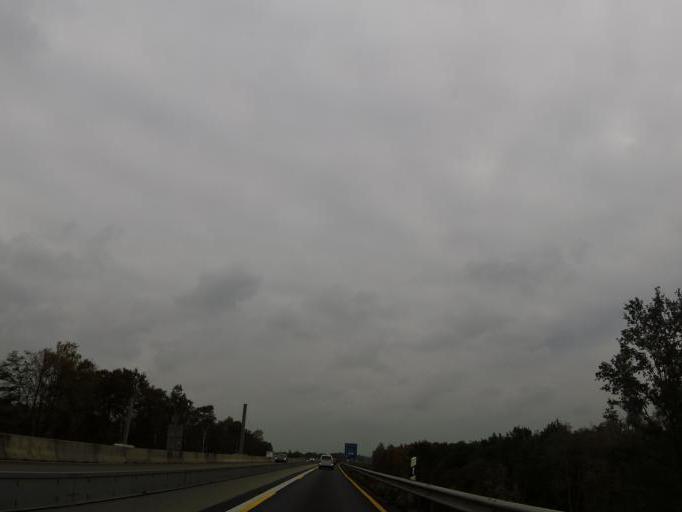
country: DE
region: Rheinland-Pfalz
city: Landstuhl
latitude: 49.4211
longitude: 7.5498
